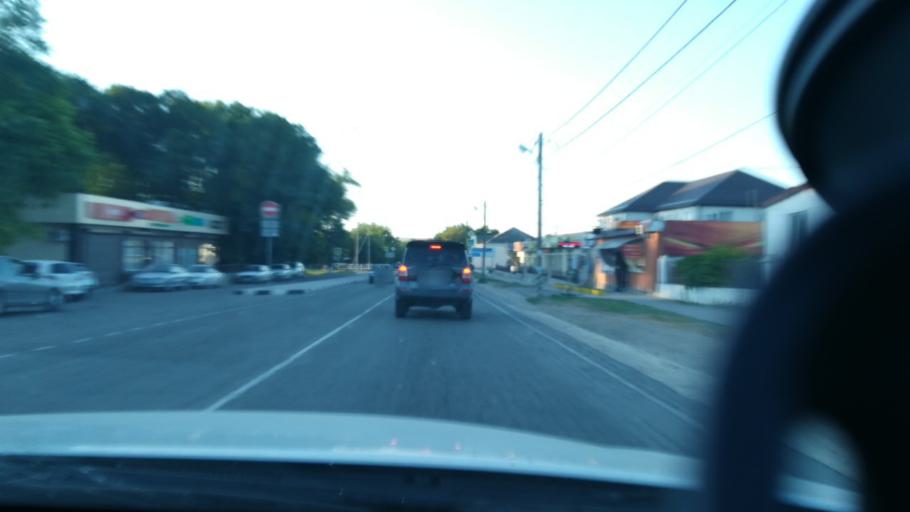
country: RU
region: Krasnodarskiy
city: Gostagayevskaya
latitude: 45.0244
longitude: 37.5031
